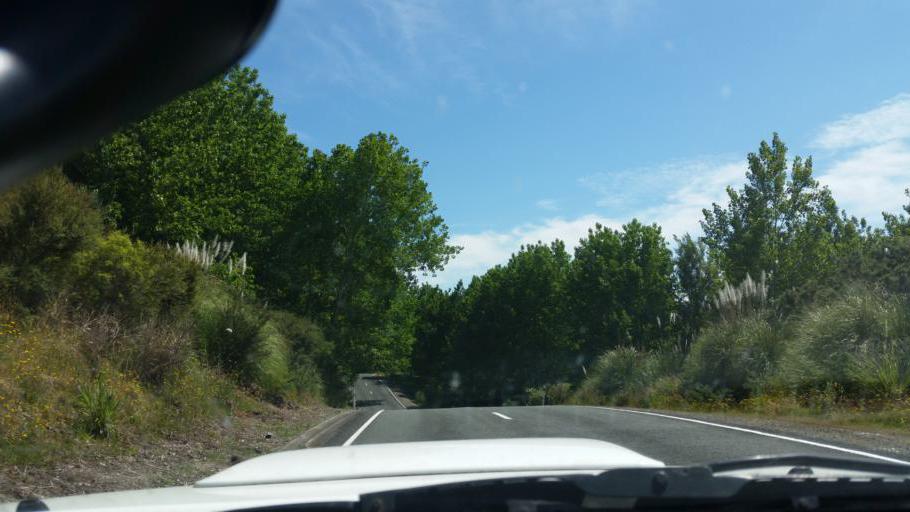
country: NZ
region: Auckland
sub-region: Auckland
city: Wellsford
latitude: -36.2121
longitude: 174.3913
